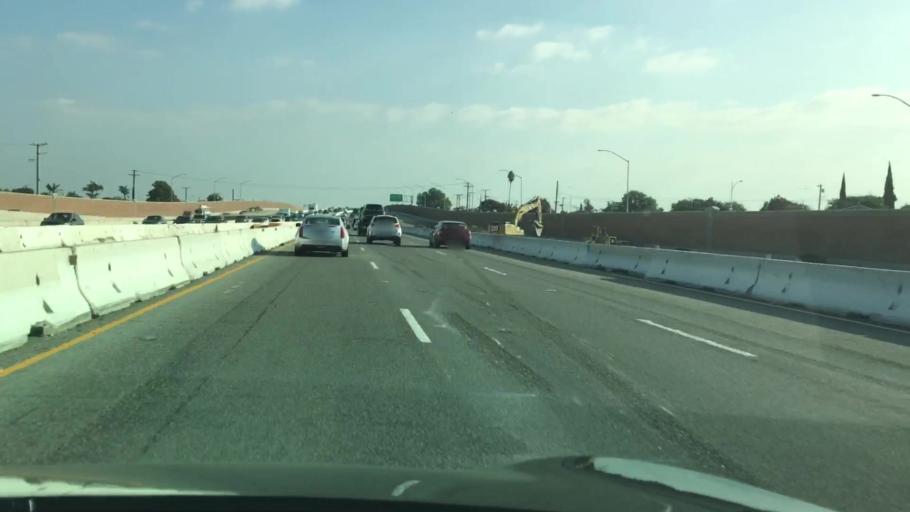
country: US
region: California
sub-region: Los Angeles County
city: Santa Fe Springs
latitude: 33.9356
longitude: -118.0930
